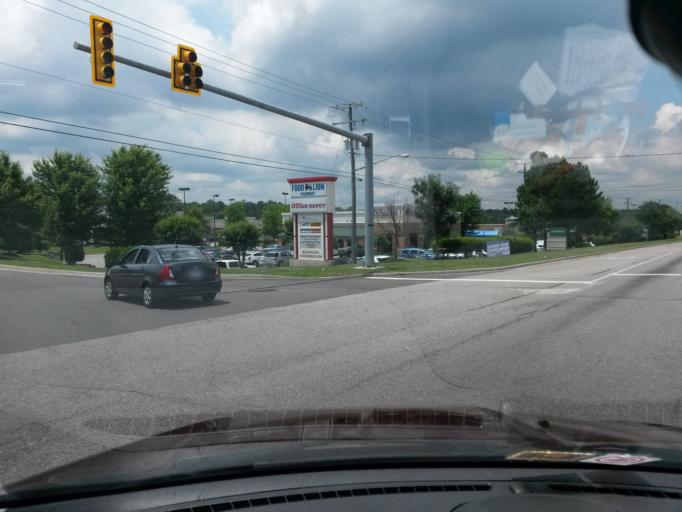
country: US
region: Virginia
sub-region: Chesterfield County
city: Chester
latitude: 37.3585
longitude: -77.4147
